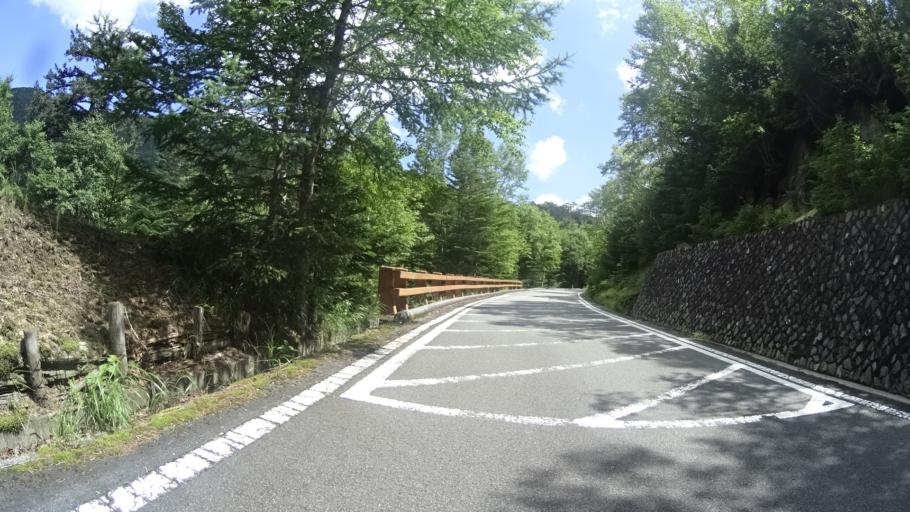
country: JP
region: Yamanashi
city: Enzan
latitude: 35.8671
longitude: 138.6592
